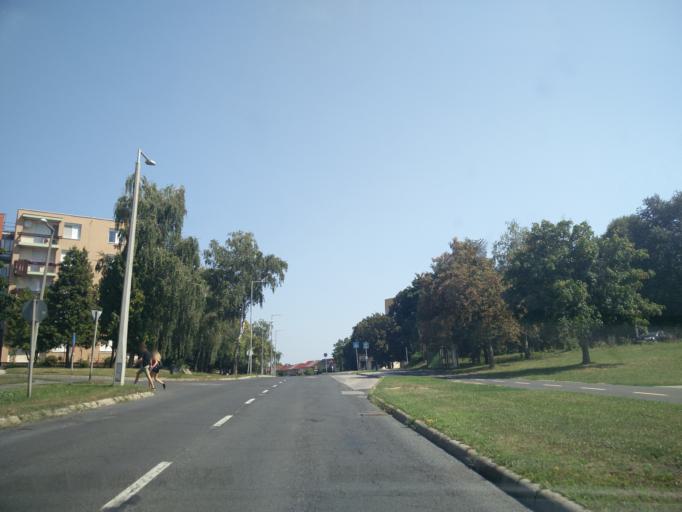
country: HU
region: Zala
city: Zalaegerszeg
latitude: 46.8262
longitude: 16.8317
